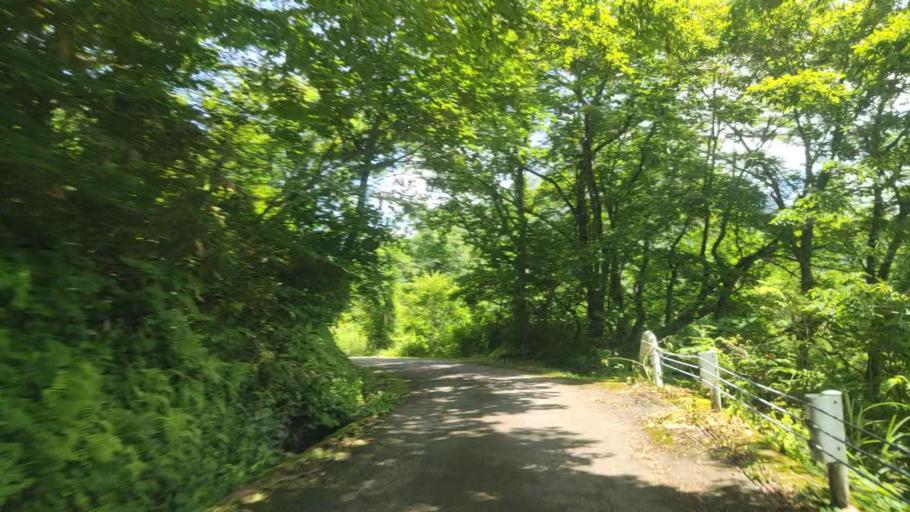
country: JP
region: Fukui
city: Ono
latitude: 35.7937
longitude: 136.4990
